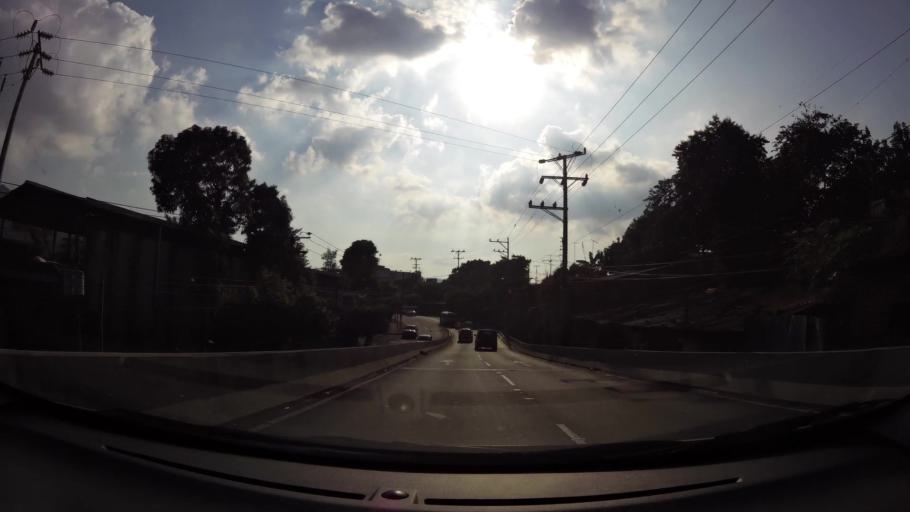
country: SV
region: San Salvador
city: San Salvador
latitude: 13.6992
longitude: -89.1739
